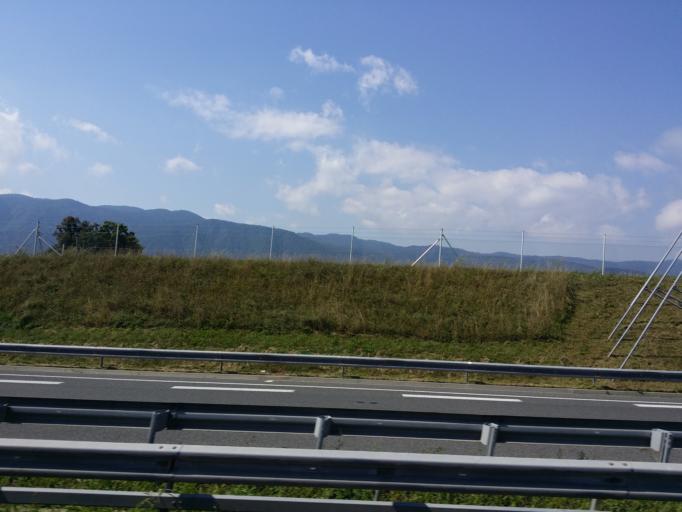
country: SI
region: Radovljica
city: Radovljica
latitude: 46.3440
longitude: 14.1854
